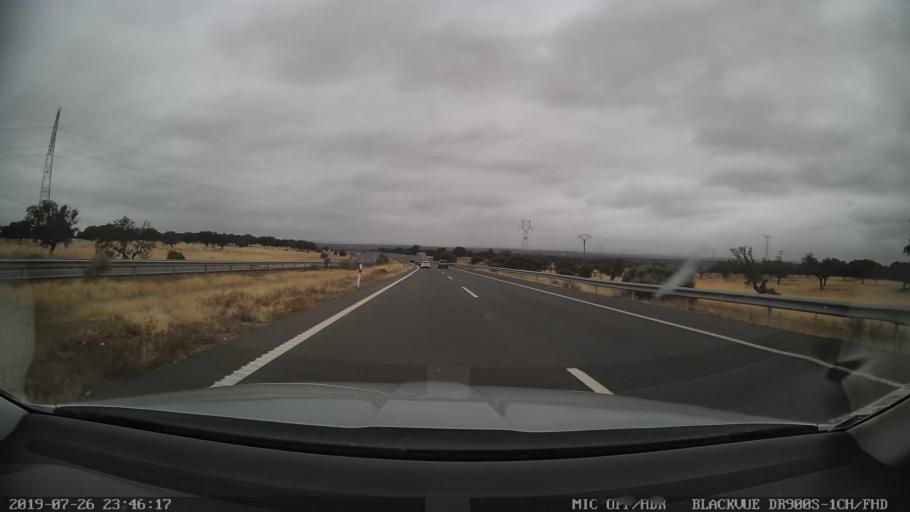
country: ES
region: Extremadura
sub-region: Provincia de Caceres
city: Jaraicejo
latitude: 39.5856
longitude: -5.8350
